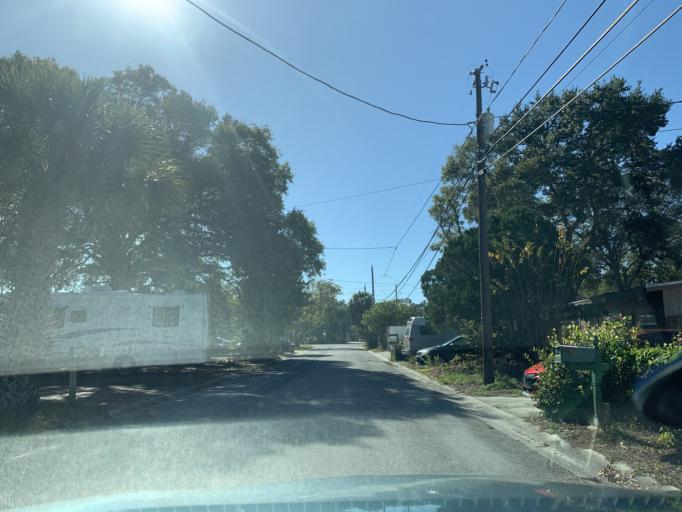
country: US
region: Florida
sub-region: Pinellas County
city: Kenneth City
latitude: 27.8146
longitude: -82.7481
